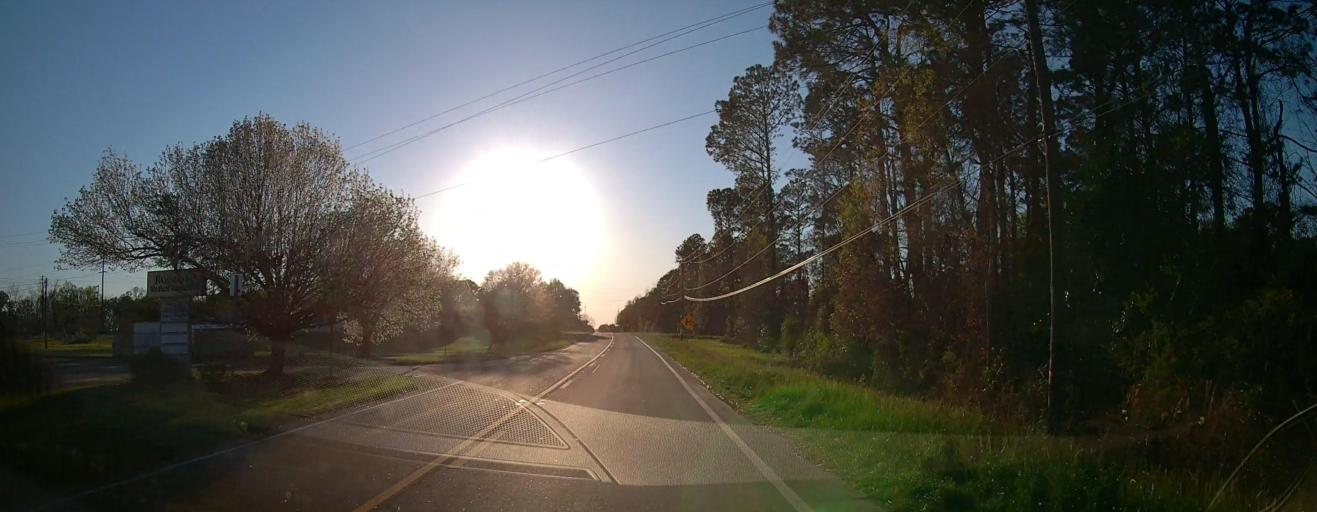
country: US
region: Georgia
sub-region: Wilcox County
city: Rochelle
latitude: 31.9509
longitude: -83.4602
